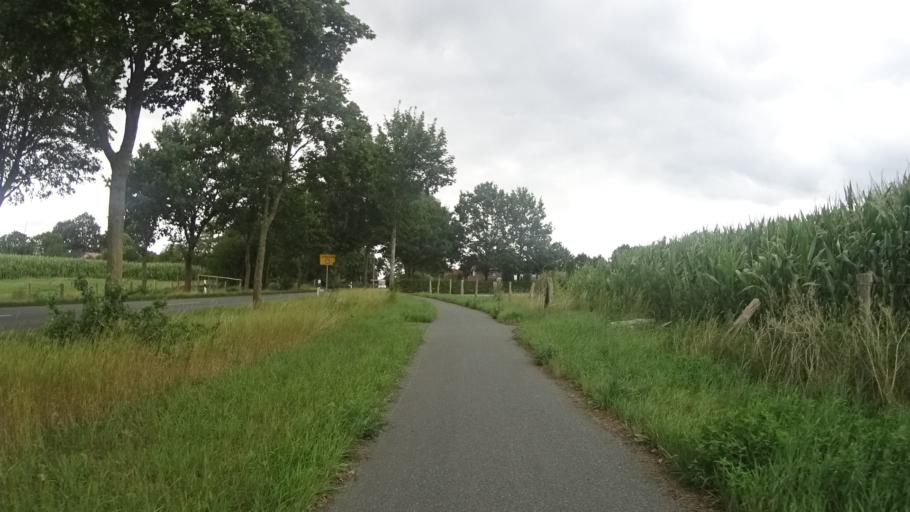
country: DE
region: Lower Saxony
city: Kuhrstedt
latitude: 53.5937
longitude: 8.8109
